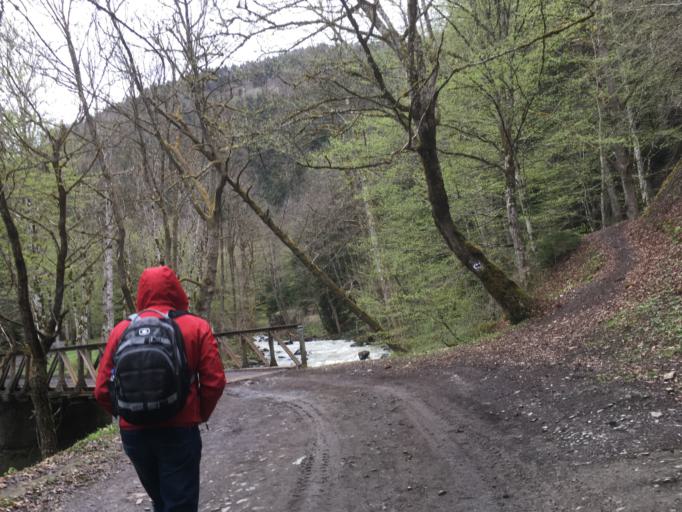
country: GE
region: Samtskhe-Javakheti
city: Borjomi
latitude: 41.8266
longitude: 43.3932
